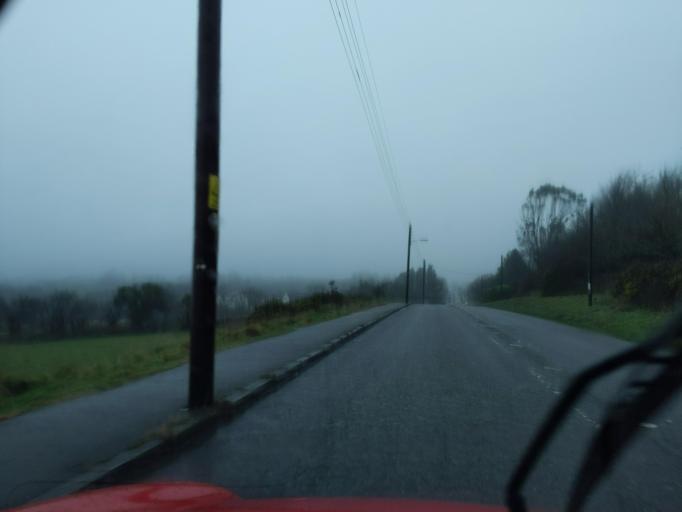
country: GB
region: England
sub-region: Cornwall
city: Callington
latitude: 50.5138
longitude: -4.3149
